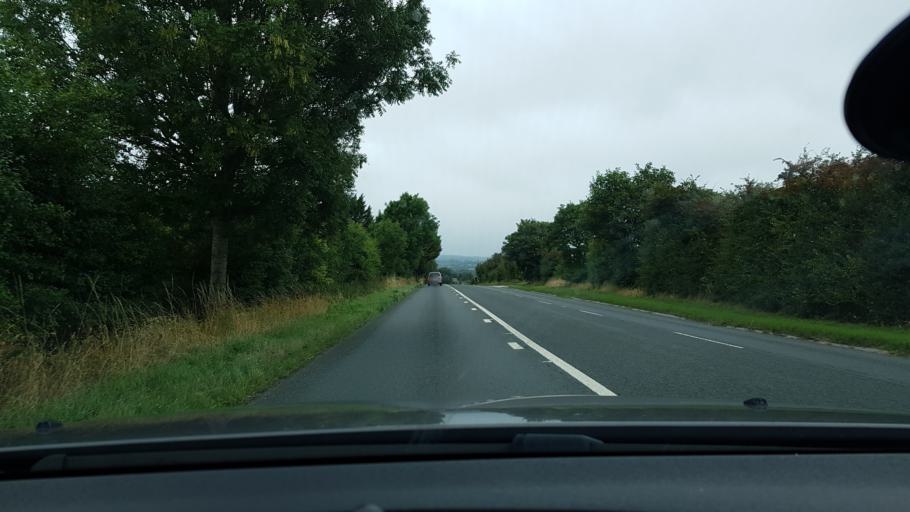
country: GB
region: England
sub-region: Wiltshire
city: Avebury
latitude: 51.4305
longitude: -1.9328
